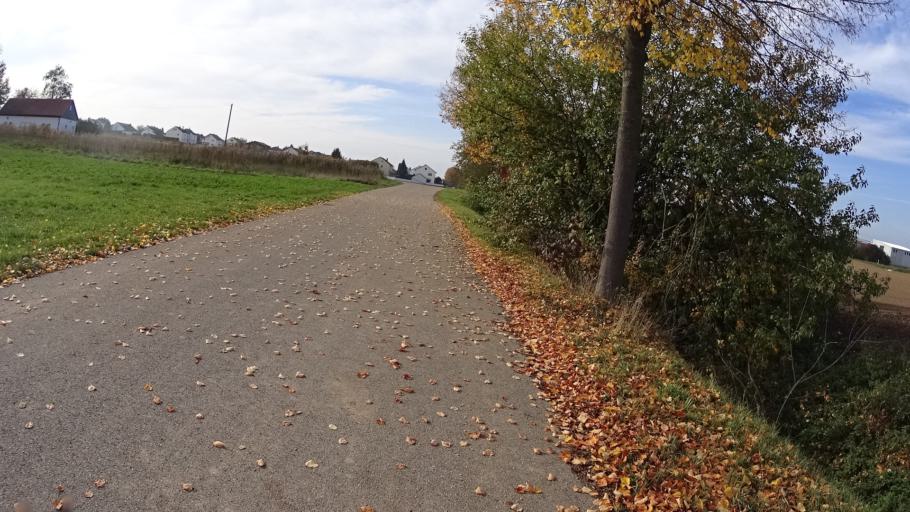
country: DE
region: Bavaria
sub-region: Upper Bavaria
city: Eitensheim
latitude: 48.8185
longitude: 11.3294
